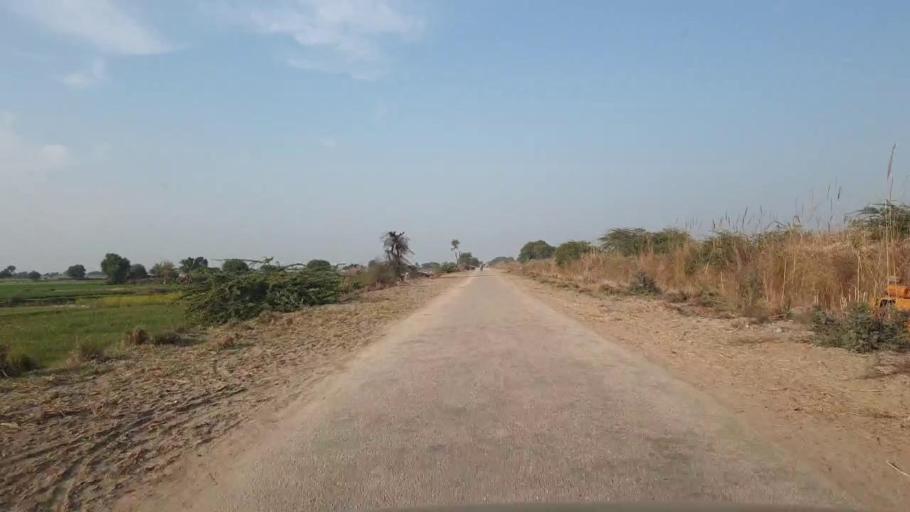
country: PK
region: Sindh
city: Shahpur Chakar
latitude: 26.1611
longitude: 68.6406
